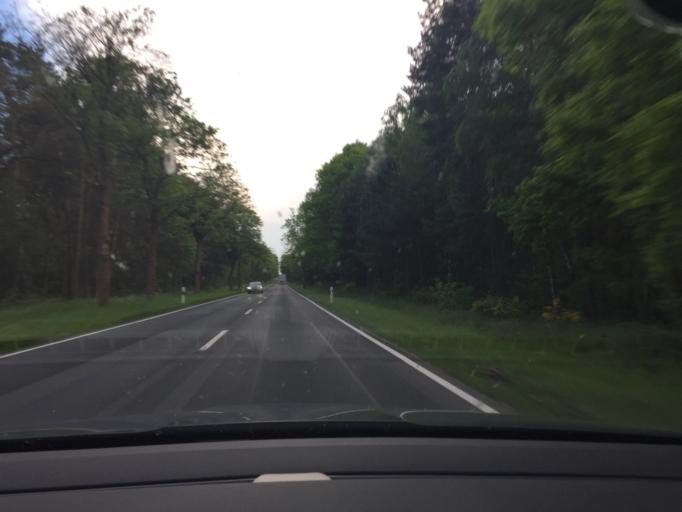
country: DE
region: Brandenburg
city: Treuenbrietzen
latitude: 52.0587
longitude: 12.8237
